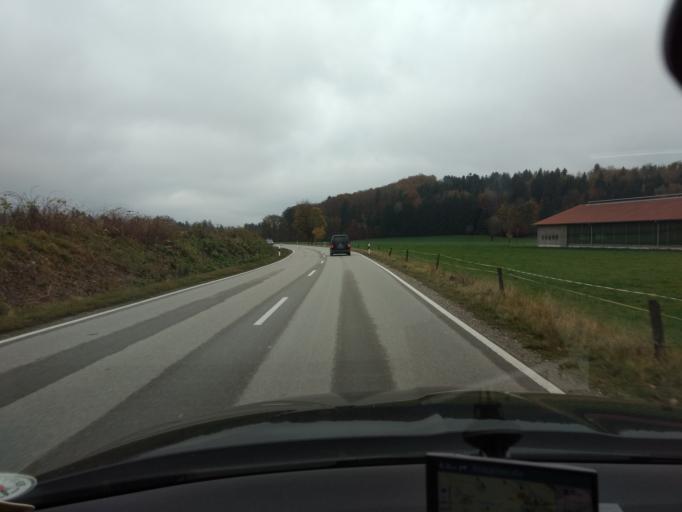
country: DE
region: Bavaria
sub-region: Upper Bavaria
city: Konigsdorf
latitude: 47.8162
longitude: 11.5168
